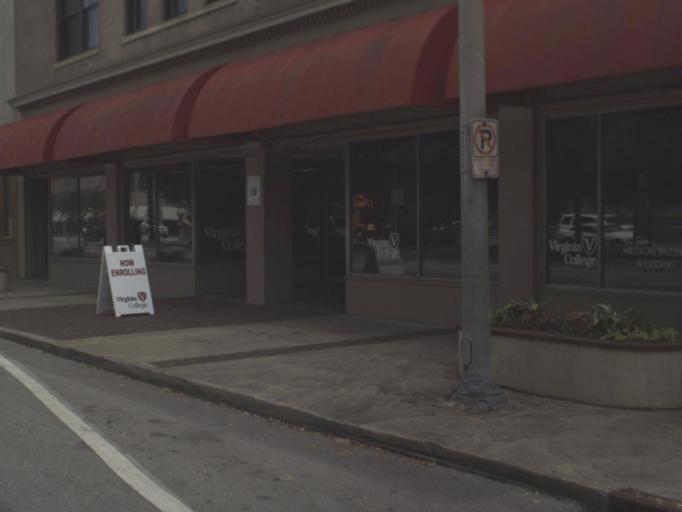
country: US
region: Florida
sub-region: Escambia County
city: Pensacola
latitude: 30.4127
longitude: -87.2163
